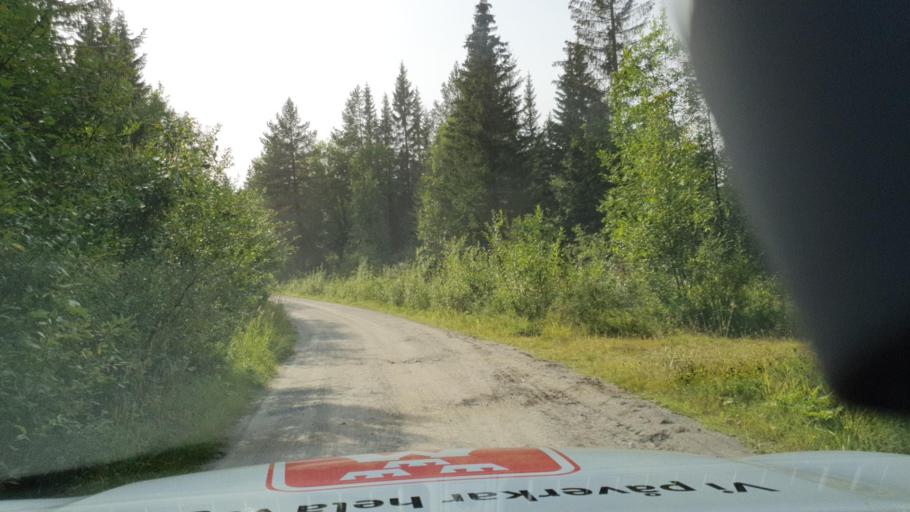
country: SE
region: Jaemtland
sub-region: OEstersunds Kommun
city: Brunflo
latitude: 63.1086
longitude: 14.8409
